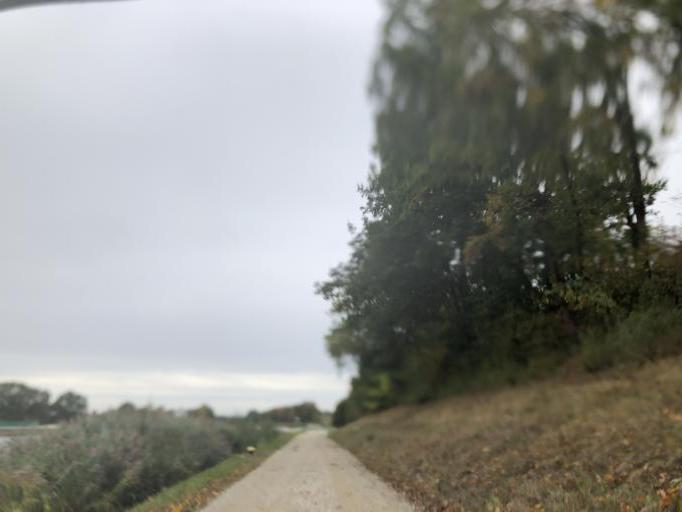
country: DE
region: Bavaria
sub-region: Regierungsbezirk Mittelfranken
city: Obermichelbach
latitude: 49.5325
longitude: 10.9637
